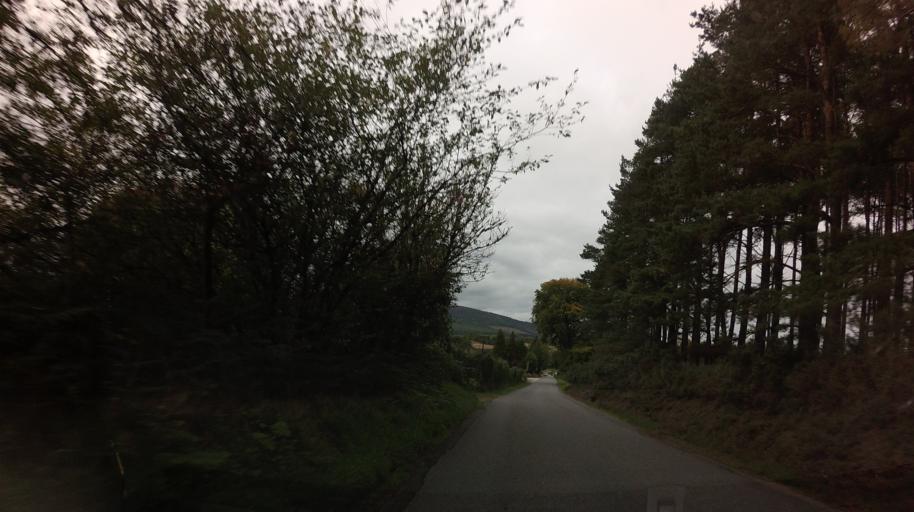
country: GB
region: Scotland
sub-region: Aberdeenshire
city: Banchory
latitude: 57.0792
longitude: -2.4596
